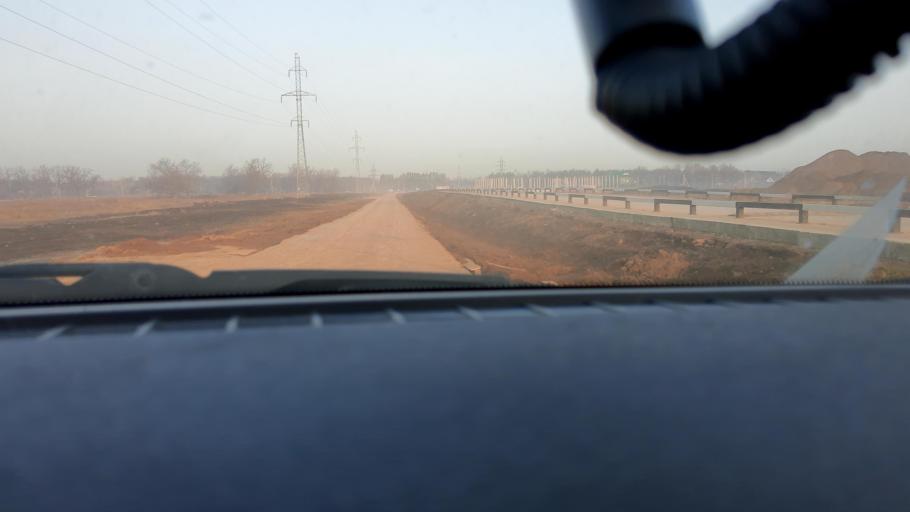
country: RU
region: Bashkortostan
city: Ufa
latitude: 54.7784
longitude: 55.9591
